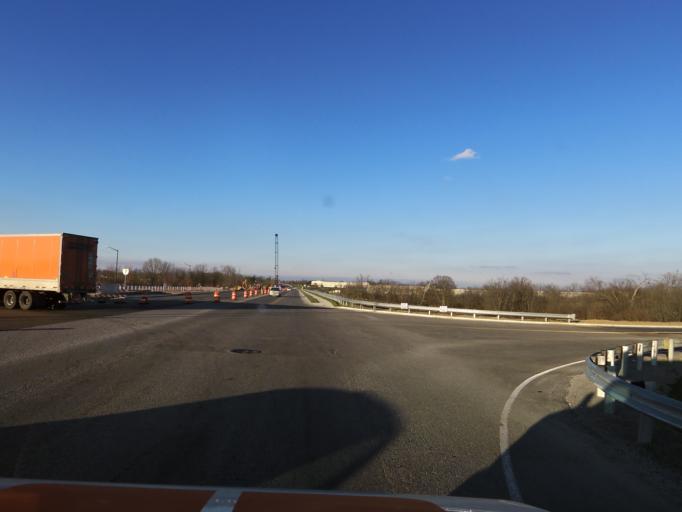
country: US
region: Kentucky
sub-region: Shelby County
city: Simpsonville
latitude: 38.2104
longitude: -85.3468
